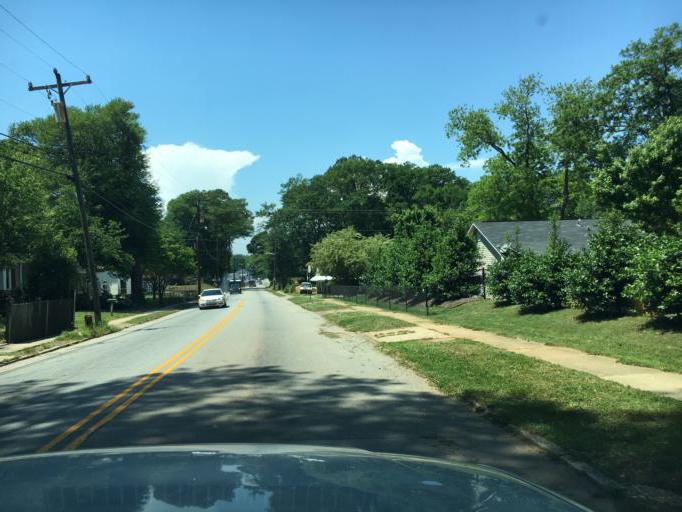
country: US
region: South Carolina
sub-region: Spartanburg County
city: Saxon
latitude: 34.9621
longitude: -81.9508
